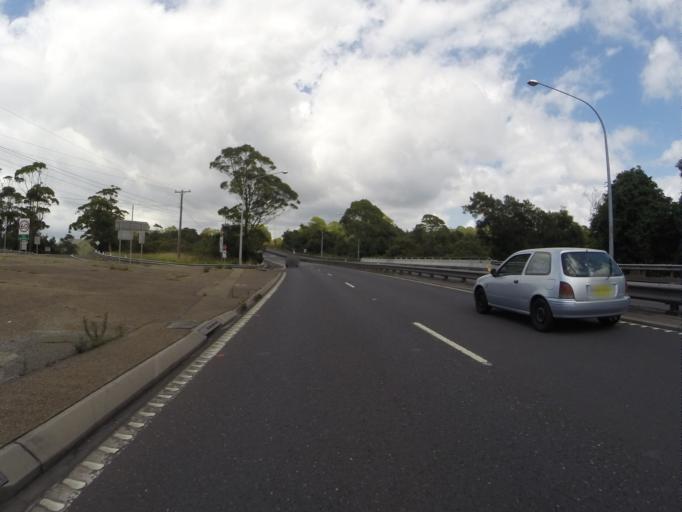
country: AU
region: New South Wales
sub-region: Wollongong
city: Bulli
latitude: -34.3104
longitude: 150.8985
